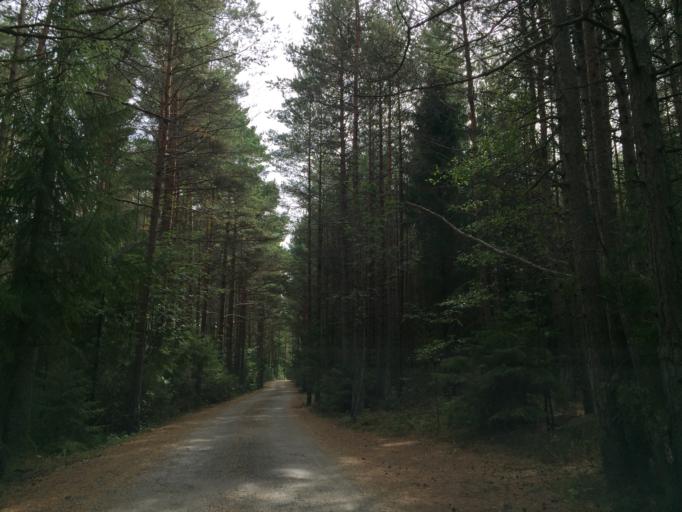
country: NO
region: Ostfold
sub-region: Hvaler
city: Skjaerhalden
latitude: 59.0301
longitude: 11.0252
